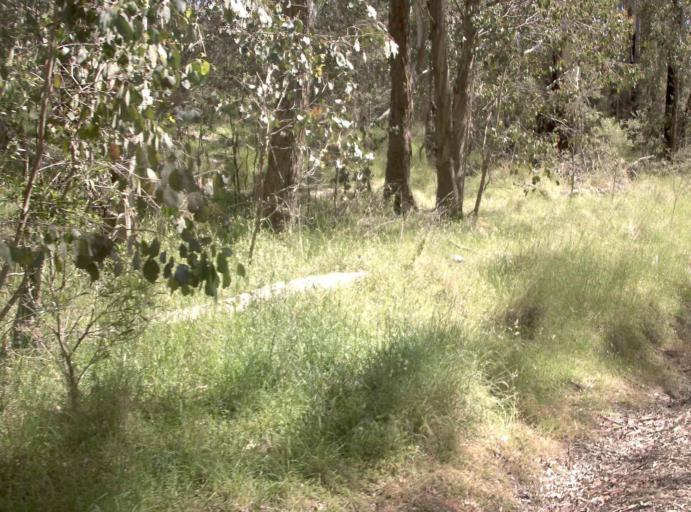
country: AU
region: New South Wales
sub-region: Bombala
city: Bombala
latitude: -37.0639
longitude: 148.7991
